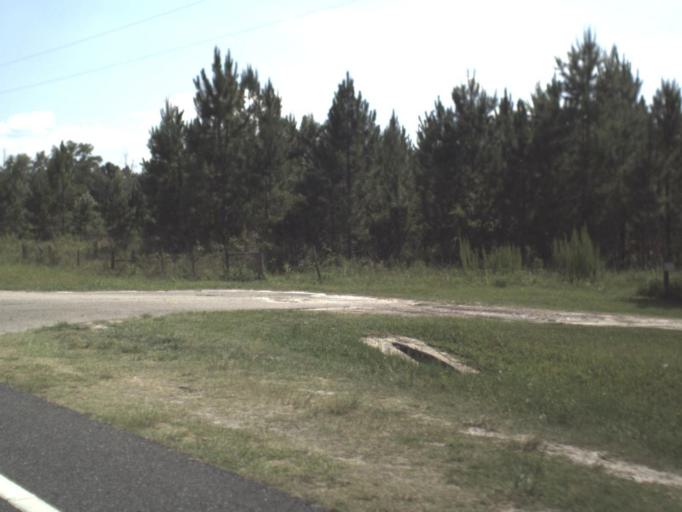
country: US
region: Florida
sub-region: Alachua County
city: Waldo
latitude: 29.7335
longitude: -82.1413
